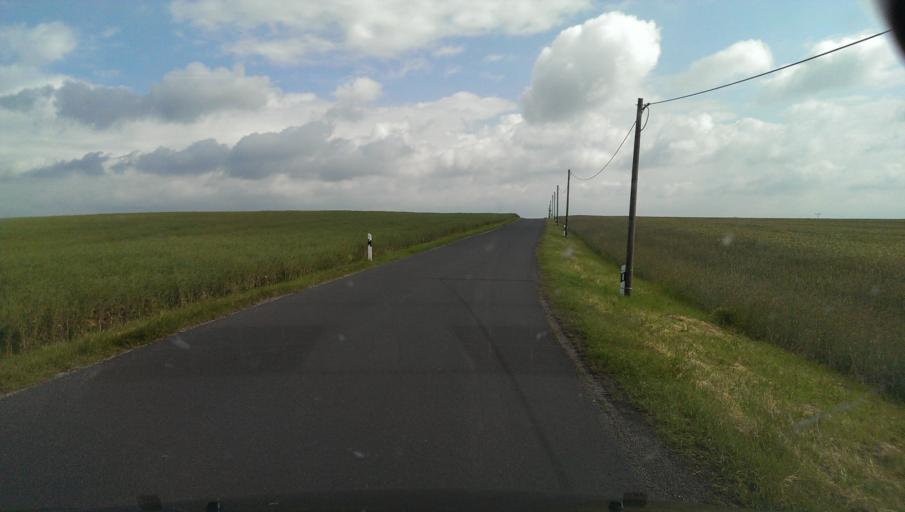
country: DE
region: Thuringia
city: Rittersdorf
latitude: 50.8217
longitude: 11.2369
